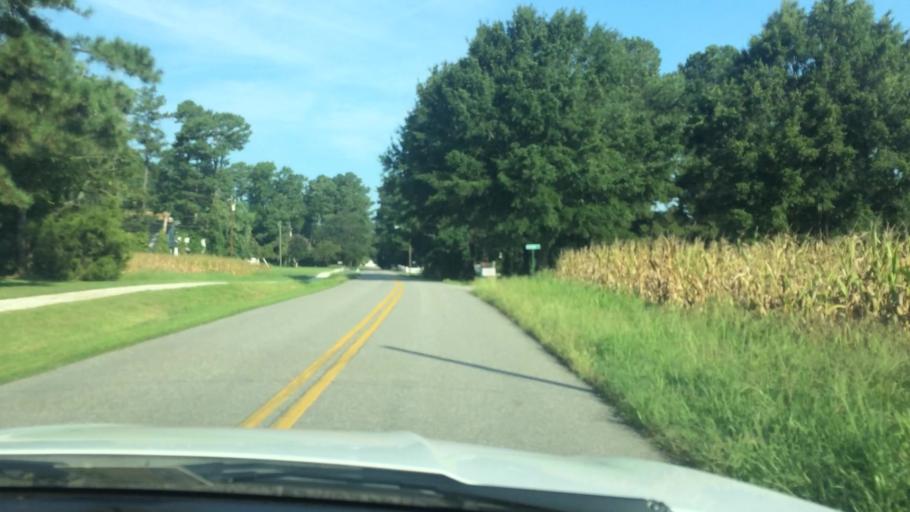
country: US
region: Virginia
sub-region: King William County
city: West Point
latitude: 37.5635
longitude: -76.7983
